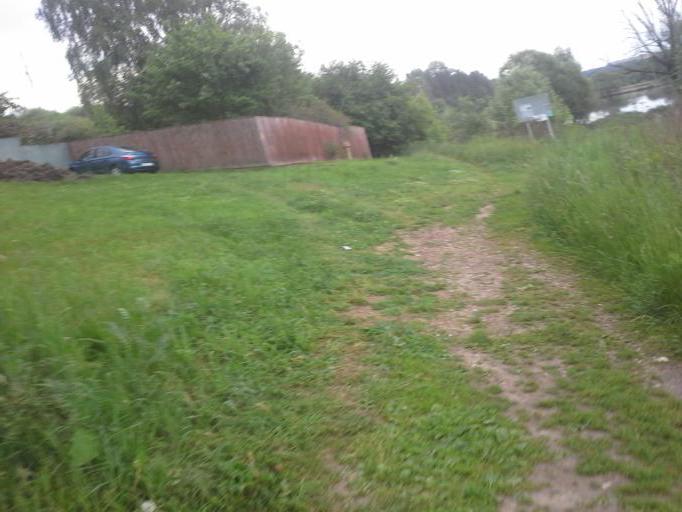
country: RU
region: Moskovskaya
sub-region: Leninskiy Rayon
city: Vnukovo
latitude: 55.6188
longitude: 37.3034
